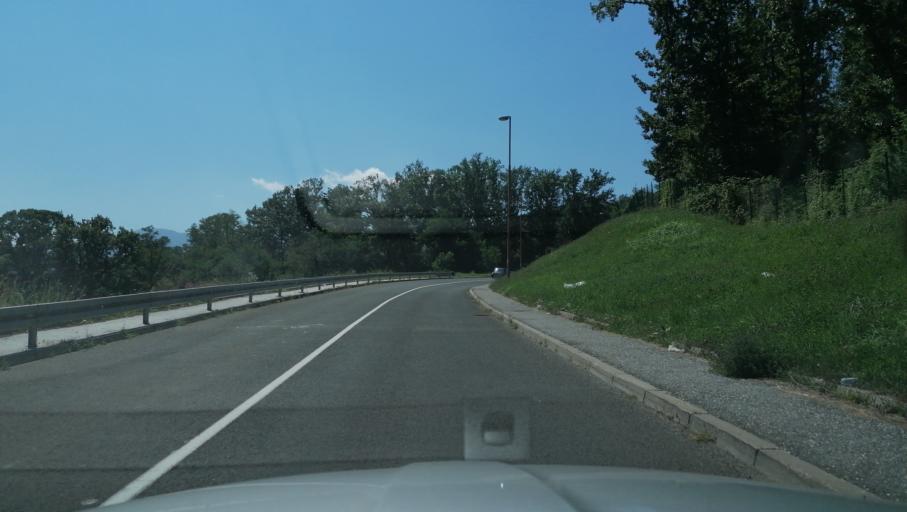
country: RS
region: Central Serbia
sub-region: Raski Okrug
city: Kraljevo
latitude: 43.6925
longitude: 20.6451
